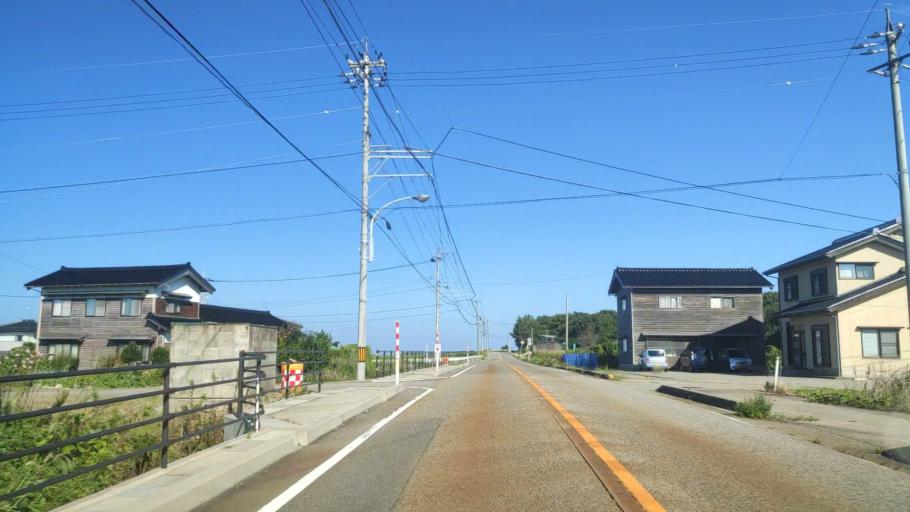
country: JP
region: Ishikawa
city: Hakui
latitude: 36.9275
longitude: 136.7587
